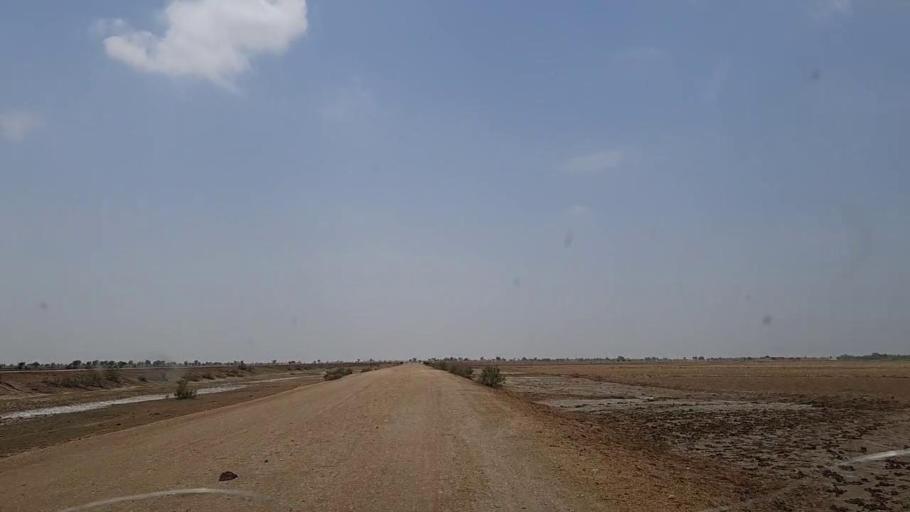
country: PK
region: Sindh
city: Phulji
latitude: 26.7933
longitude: 67.6411
